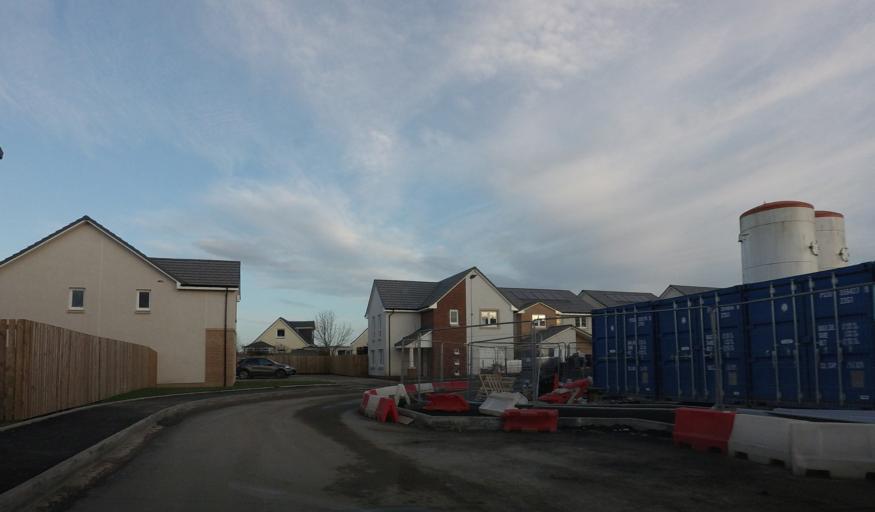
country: GB
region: Scotland
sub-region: Perth and Kinross
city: Bridge of Earn
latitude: 56.3387
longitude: -3.4059
